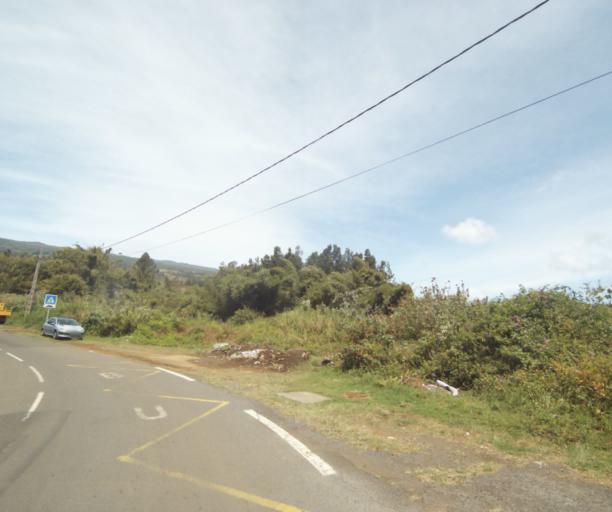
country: RE
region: Reunion
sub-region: Reunion
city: Trois-Bassins
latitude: -21.0671
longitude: 55.3080
